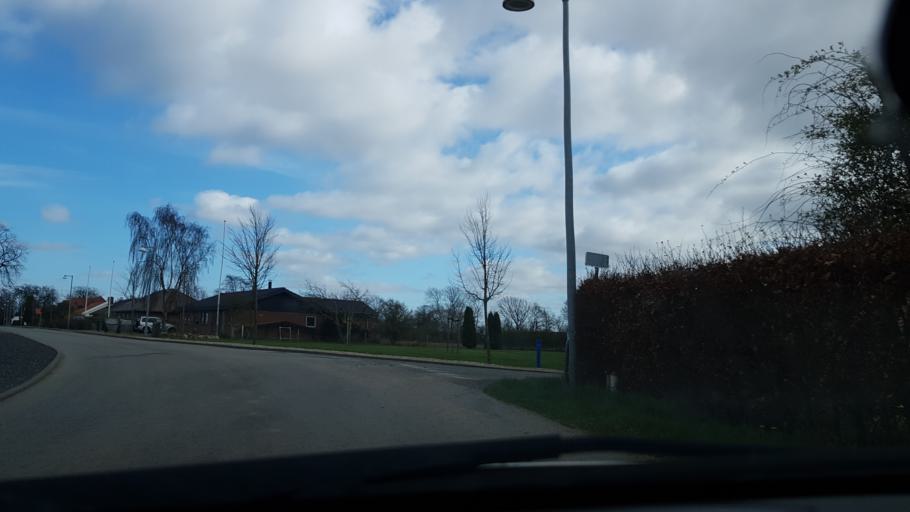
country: DK
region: South Denmark
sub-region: Vejen Kommune
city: Rodding
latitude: 55.4216
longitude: 9.0943
